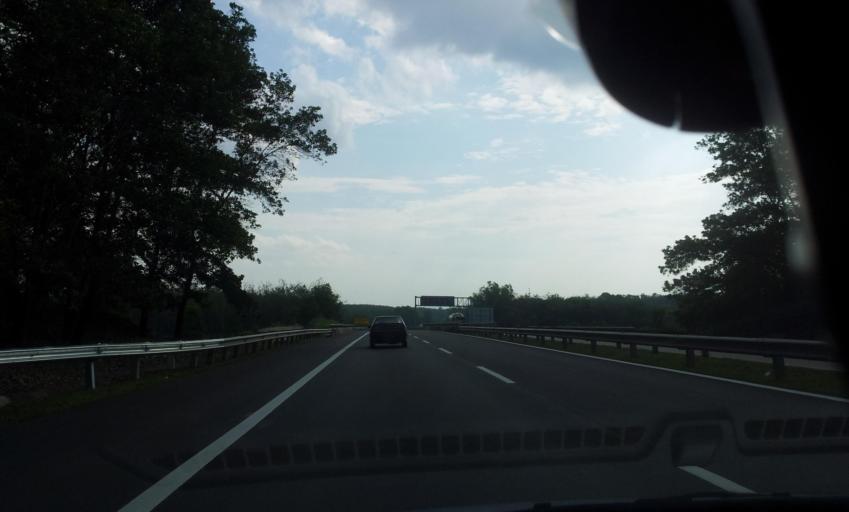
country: MY
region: Pahang
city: Mentekab
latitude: 3.5071
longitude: 102.3994
